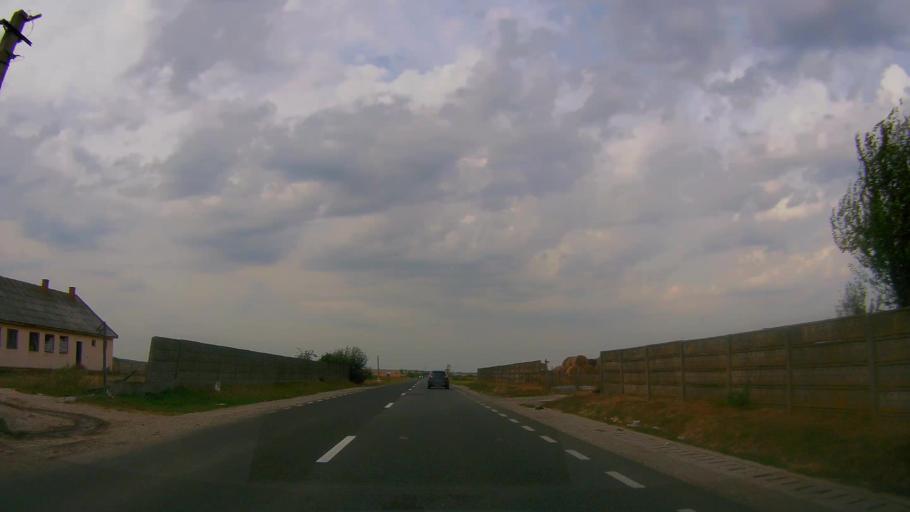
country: RO
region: Satu Mare
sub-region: Comuna Beltiug
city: Beltiug
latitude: 47.5767
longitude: 22.8805
